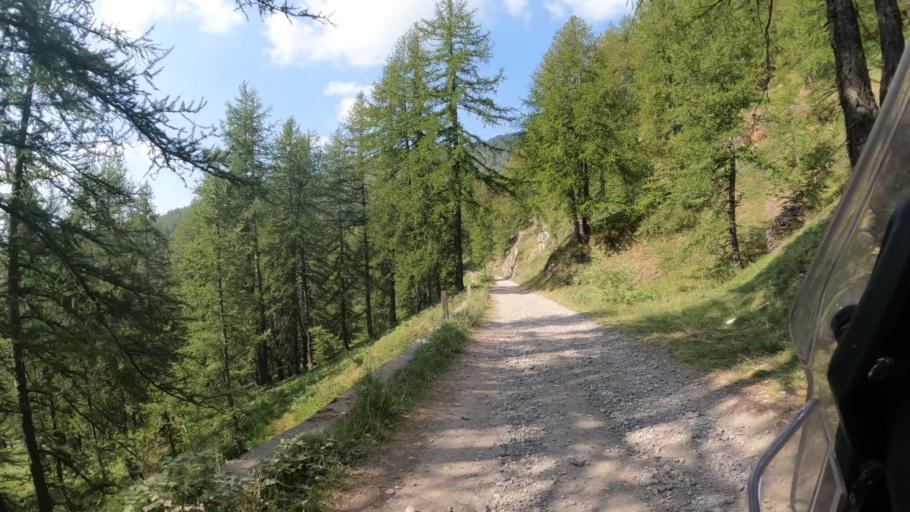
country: IT
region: Piedmont
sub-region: Provincia di Cuneo
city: Briga Alta
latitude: 44.1007
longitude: 7.7182
